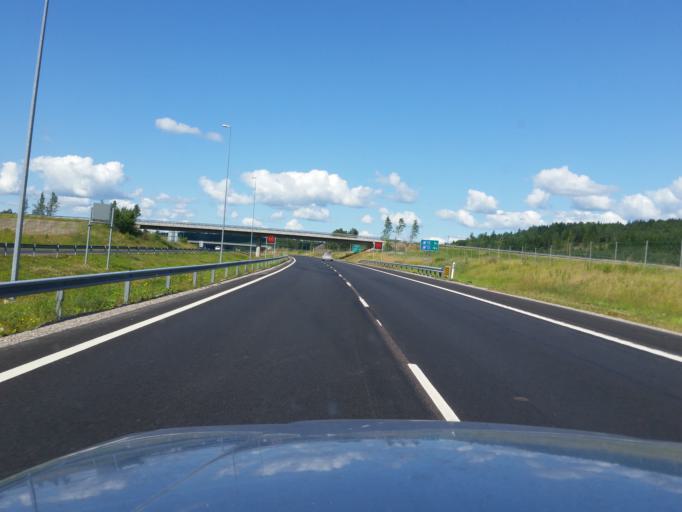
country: FI
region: Varsinais-Suomi
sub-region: Salo
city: Muurla
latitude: 60.3848
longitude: 23.3081
